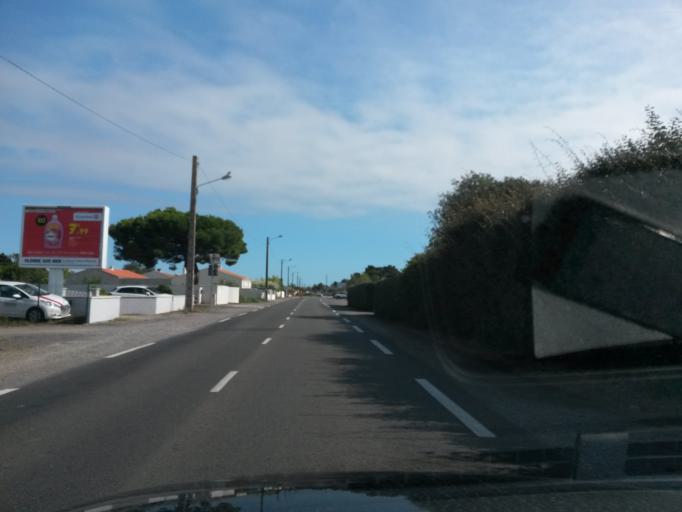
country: FR
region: Pays de la Loire
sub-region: Departement de la Vendee
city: Olonne-sur-Mer
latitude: 46.5486
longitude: -1.8058
